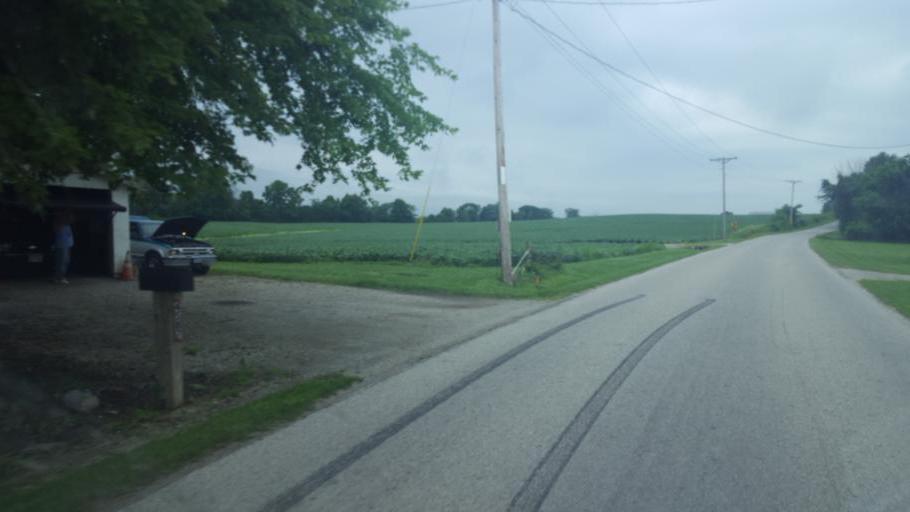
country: US
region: Ohio
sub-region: Knox County
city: Centerburg
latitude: 40.3574
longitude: -82.8033
